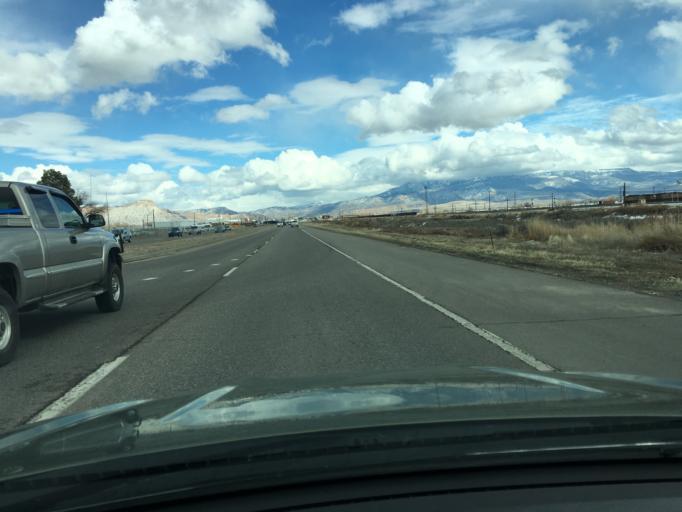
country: US
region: Colorado
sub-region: Mesa County
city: Grand Junction
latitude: 39.0690
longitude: -108.5336
